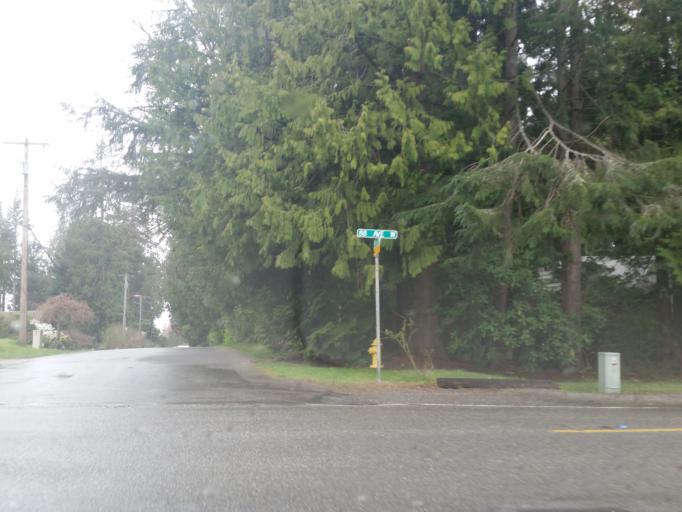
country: US
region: Washington
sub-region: Snohomish County
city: Meadowdale
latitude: 47.8324
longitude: -122.3522
